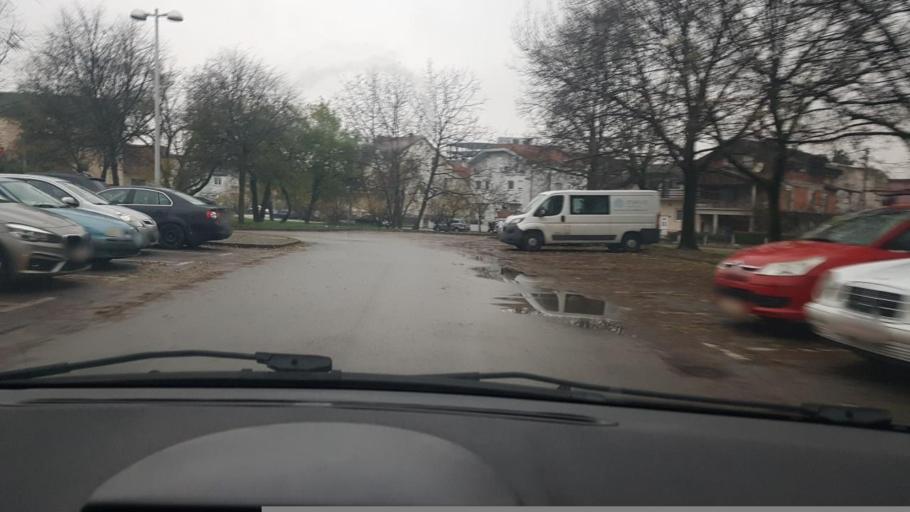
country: HR
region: Grad Zagreb
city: Jankomir
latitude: 45.7936
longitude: 15.9277
